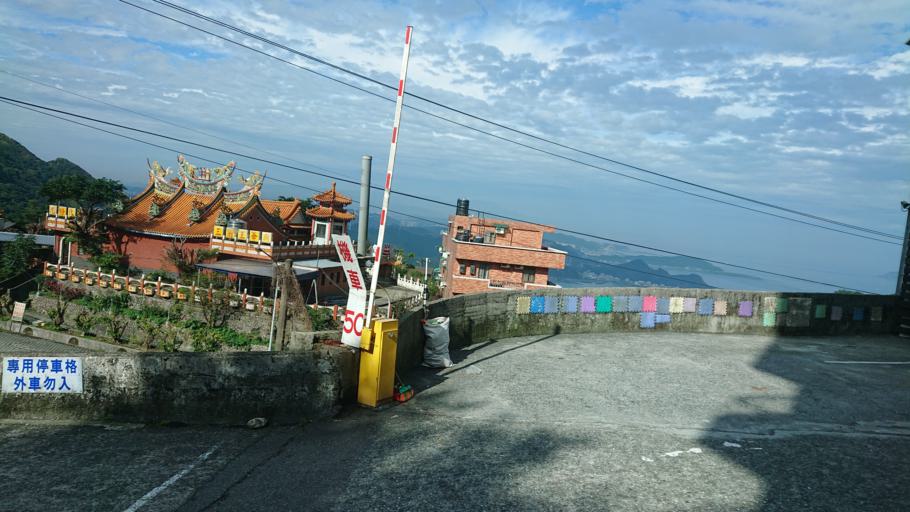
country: TW
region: Taiwan
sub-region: Keelung
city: Keelung
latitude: 25.1110
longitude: 121.8459
